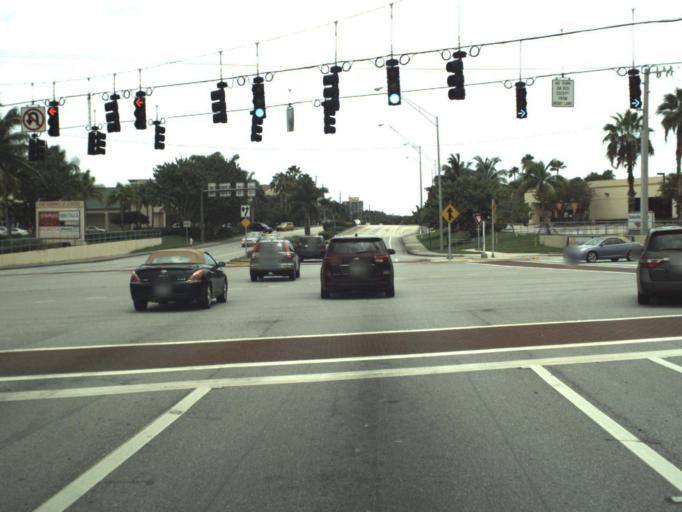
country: US
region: Florida
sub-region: Palm Beach County
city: Jupiter
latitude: 26.9338
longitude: -80.0812
